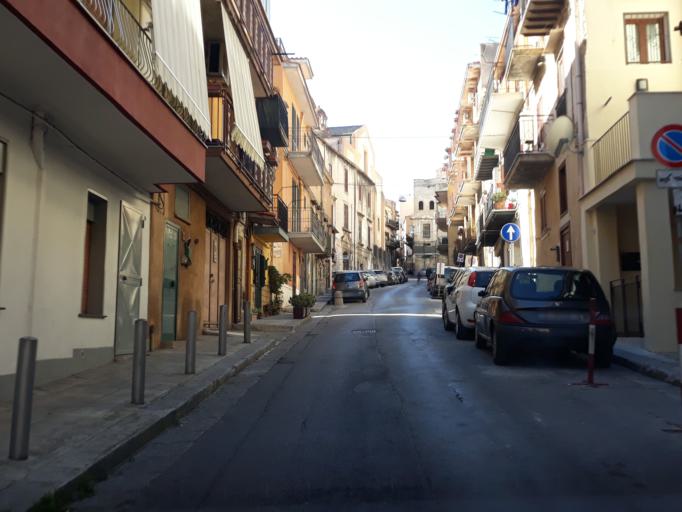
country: IT
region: Sicily
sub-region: Palermo
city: Monreale
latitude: 38.0843
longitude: 13.2935
